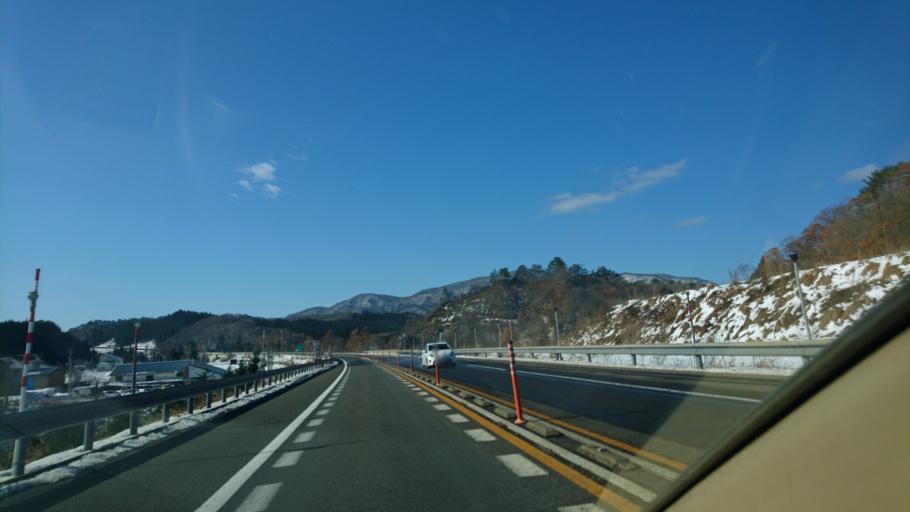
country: JP
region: Akita
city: Yokotemachi
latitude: 39.3162
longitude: 140.7579
